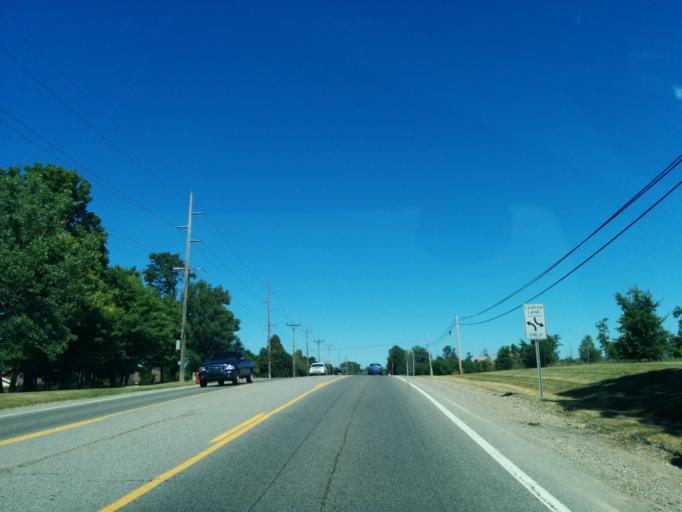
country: US
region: Michigan
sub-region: Oakland County
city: West Bloomfield Township
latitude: 42.5416
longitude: -83.4076
